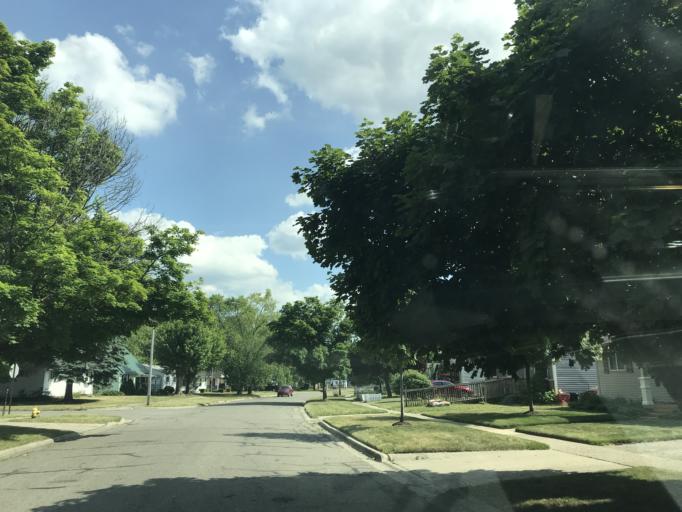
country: US
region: Michigan
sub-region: Washtenaw County
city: Ypsilanti
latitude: 42.2559
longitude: -83.5825
